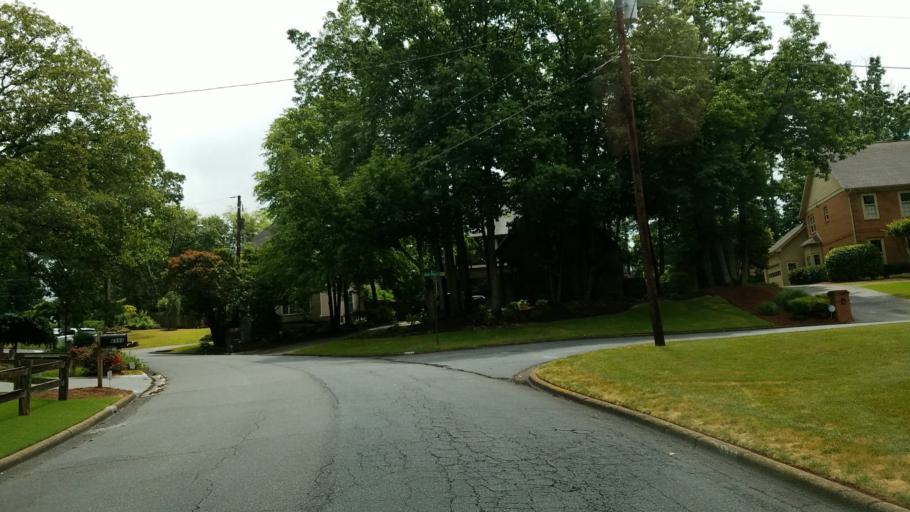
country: US
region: Georgia
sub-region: DeKalb County
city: Dunwoody
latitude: 33.9439
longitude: -84.3393
